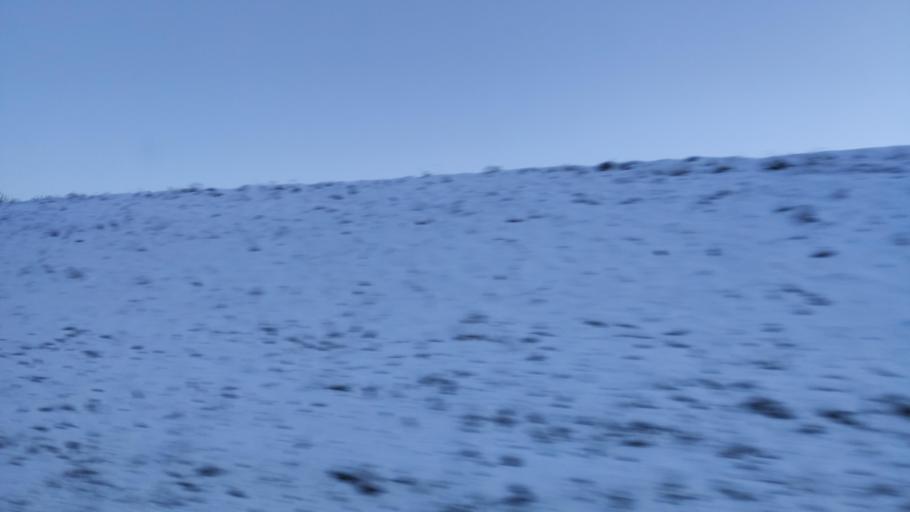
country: PL
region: Kujawsko-Pomorskie
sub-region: Powiat zninski
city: Barcin
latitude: 52.8716
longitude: 17.8482
